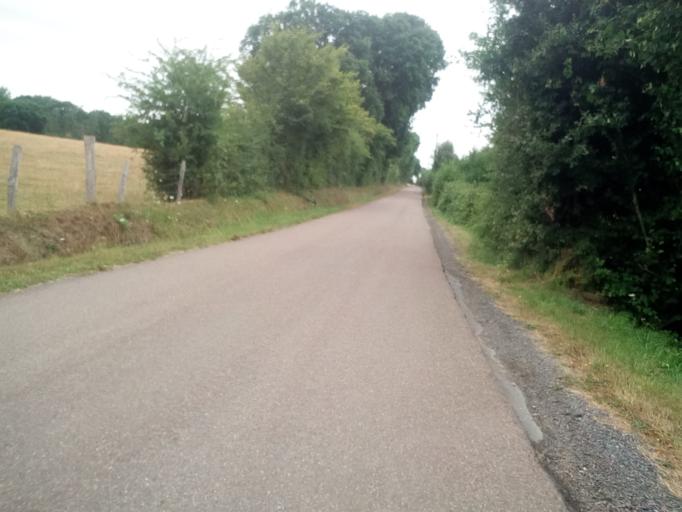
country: FR
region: Lower Normandy
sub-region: Departement du Calvados
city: Clinchamps-sur-Orne
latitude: 49.0315
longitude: -0.3939
